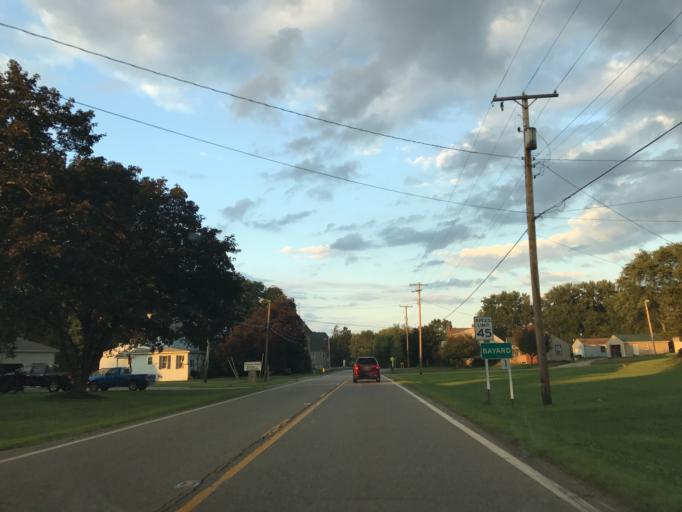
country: US
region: Ohio
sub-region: Stark County
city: Minerva
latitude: 40.7466
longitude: -81.0717
